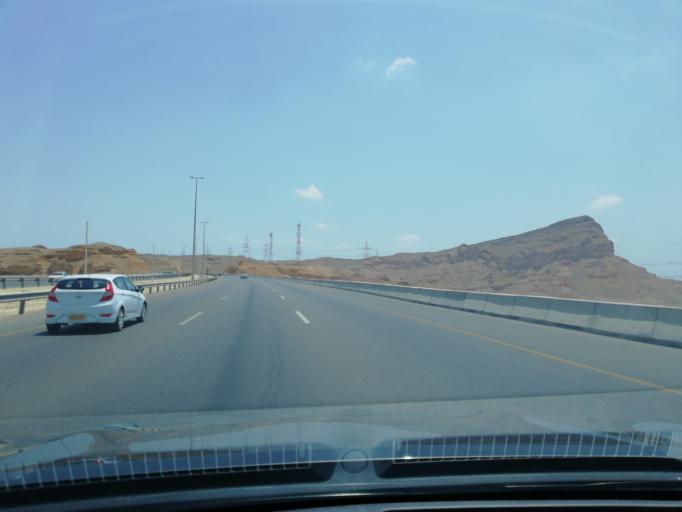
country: OM
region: Muhafazat Masqat
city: As Sib al Jadidah
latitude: 23.5414
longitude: 58.2509
